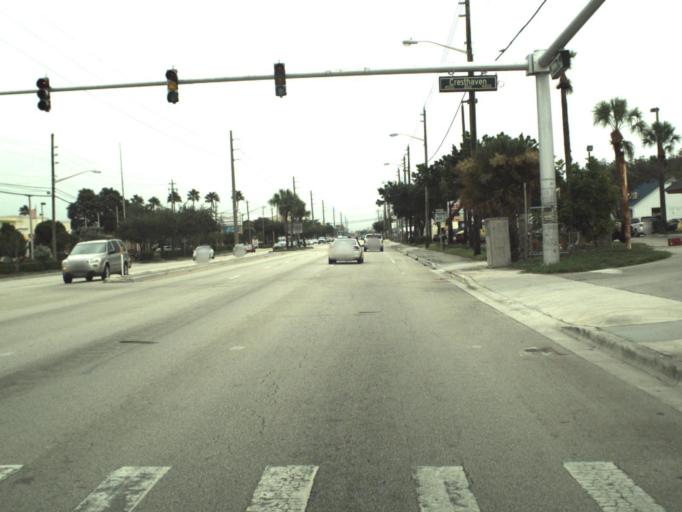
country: US
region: Florida
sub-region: Palm Beach County
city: Palm Springs
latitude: 26.6374
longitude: -80.1127
